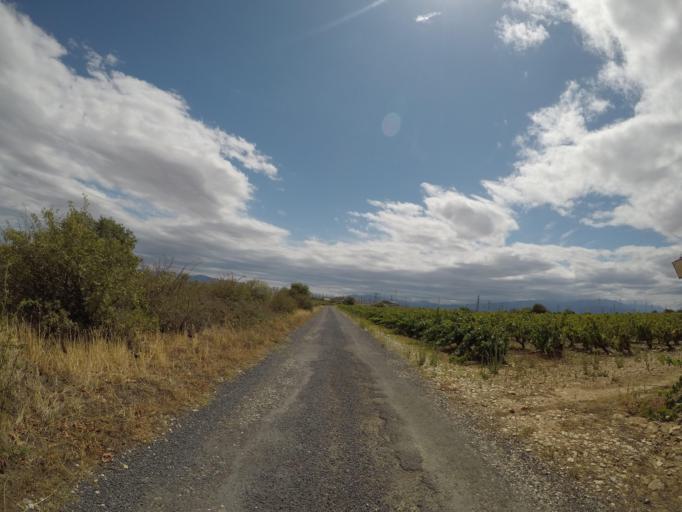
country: FR
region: Languedoc-Roussillon
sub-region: Departement des Pyrenees-Orientales
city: Baixas
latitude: 42.7384
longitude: 2.8030
